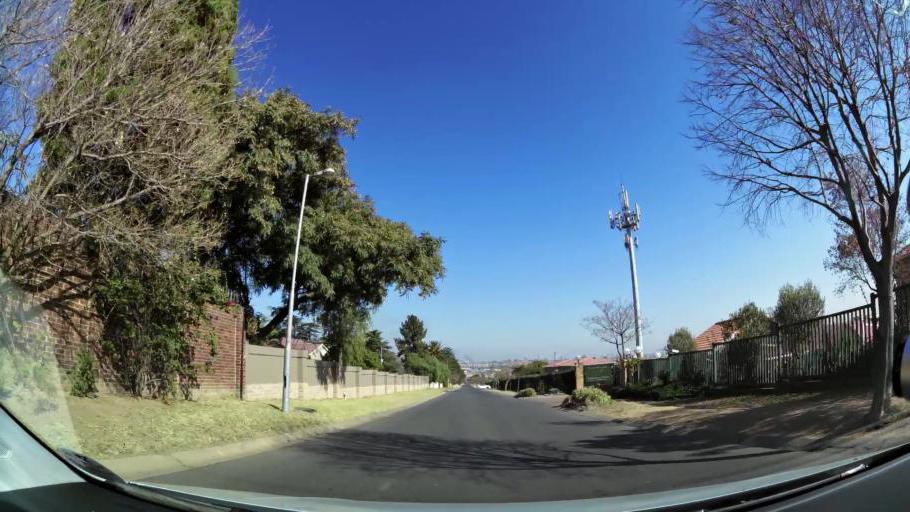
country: ZA
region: Gauteng
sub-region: City of Johannesburg Metropolitan Municipality
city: Modderfontein
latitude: -26.1124
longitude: 28.1256
